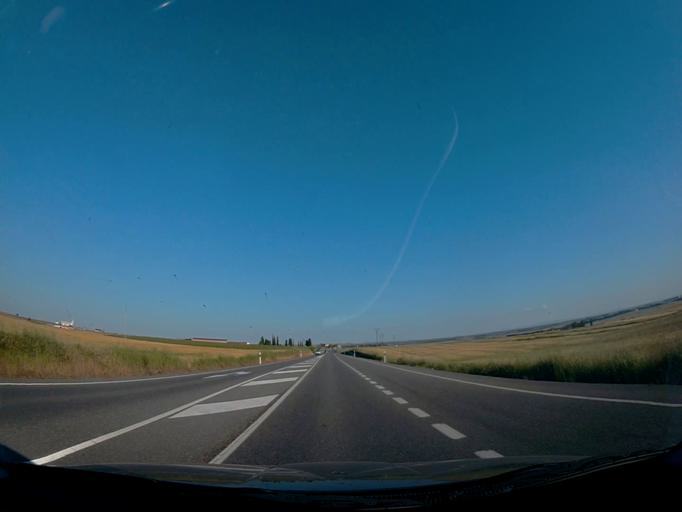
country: ES
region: Castille-La Mancha
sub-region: Province of Toledo
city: Maqueda
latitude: 40.0777
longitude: -4.3787
